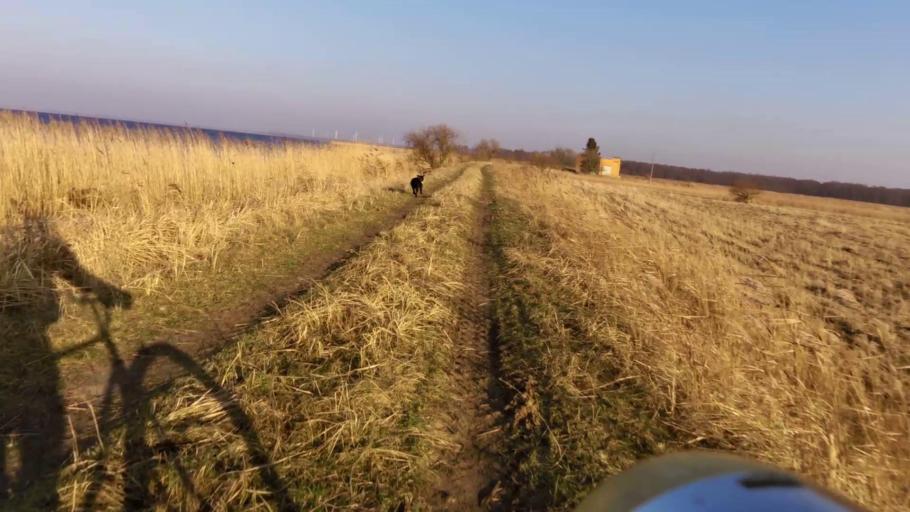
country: PL
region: West Pomeranian Voivodeship
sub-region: Powiat kamienski
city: Wolin
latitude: 53.7552
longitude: 14.5838
